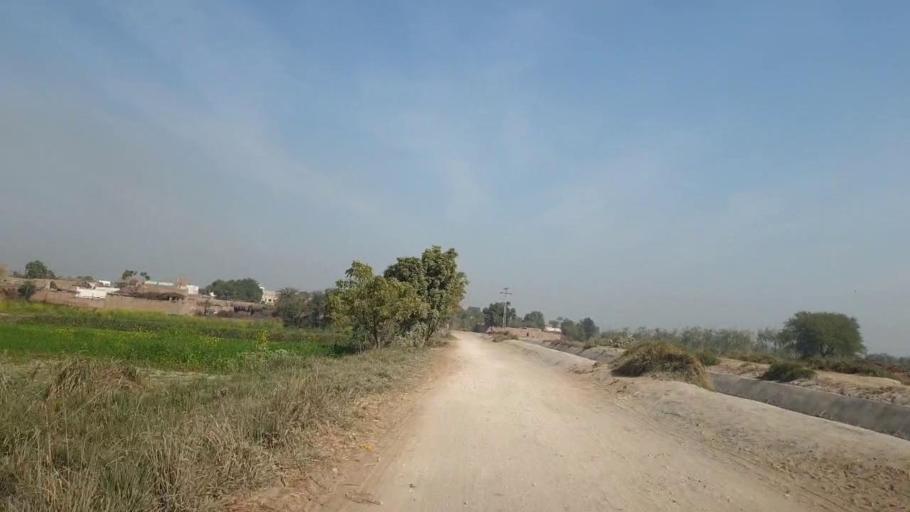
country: PK
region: Sindh
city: Tando Allahyar
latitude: 25.5987
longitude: 68.7220
